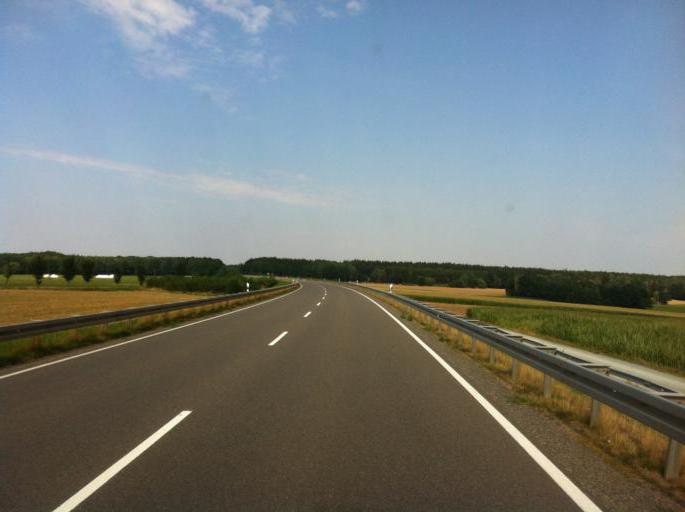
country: DE
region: Saxony
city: Reichenbach/Vogtland
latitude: 50.6237
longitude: 12.3342
